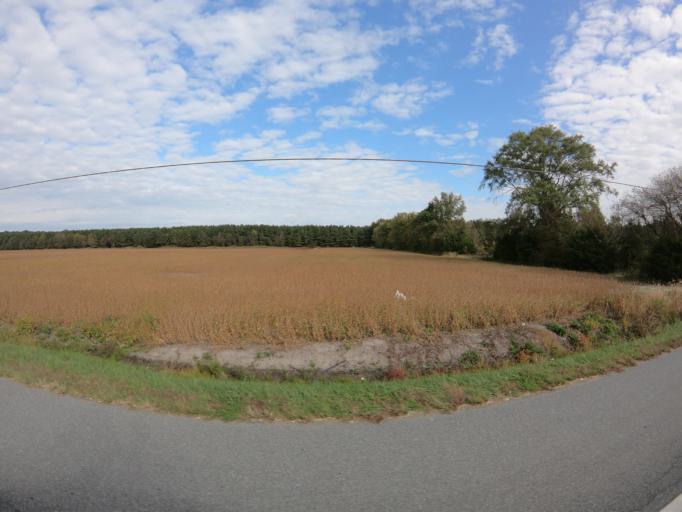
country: US
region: Delaware
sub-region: Sussex County
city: Georgetown
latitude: 38.6987
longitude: -75.4211
